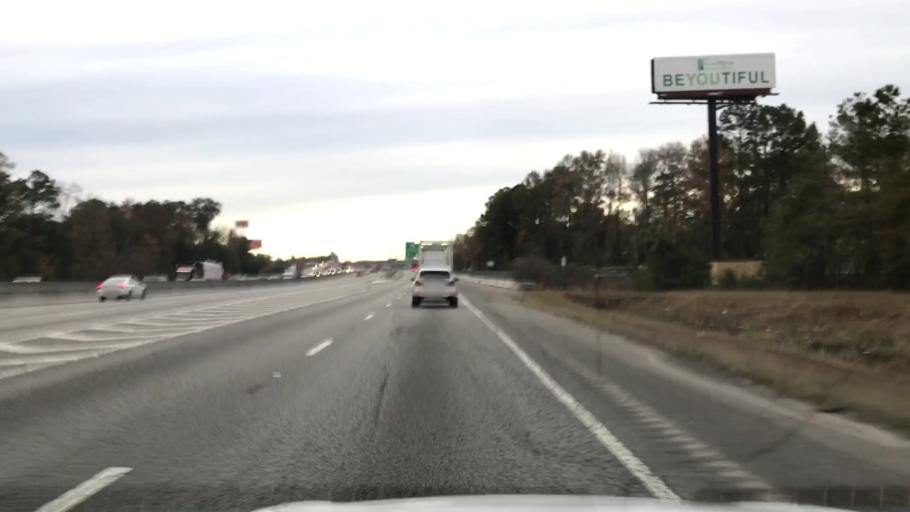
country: US
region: South Carolina
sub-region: Berkeley County
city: Hanahan
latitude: 32.9292
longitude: -80.0443
